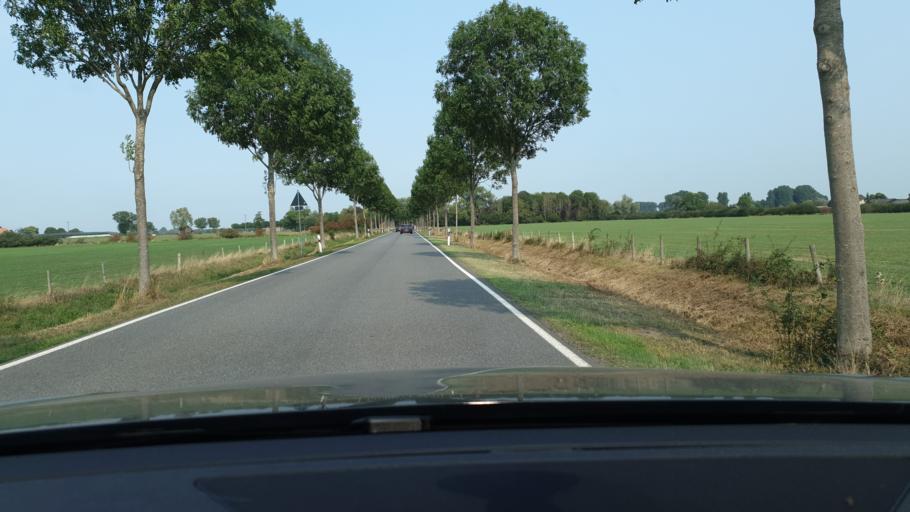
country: DE
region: North Rhine-Westphalia
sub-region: Regierungsbezirk Dusseldorf
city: Kranenburg
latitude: 51.8038
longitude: 6.0142
